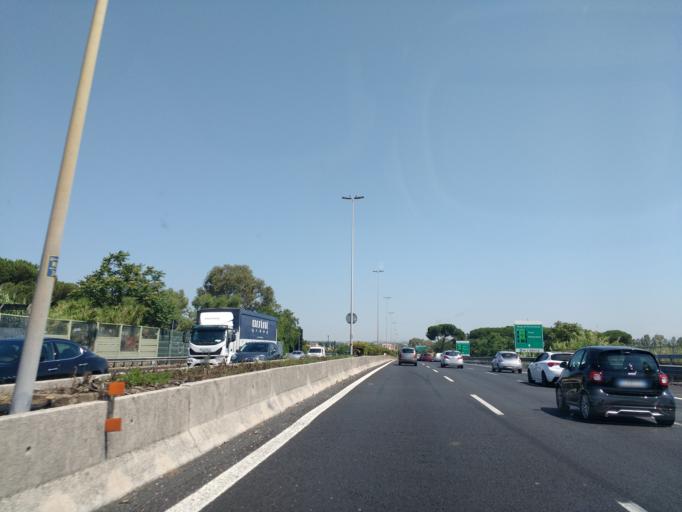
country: IT
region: Latium
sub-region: Citta metropolitana di Roma Capitale
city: Setteville
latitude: 41.9111
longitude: 12.6157
